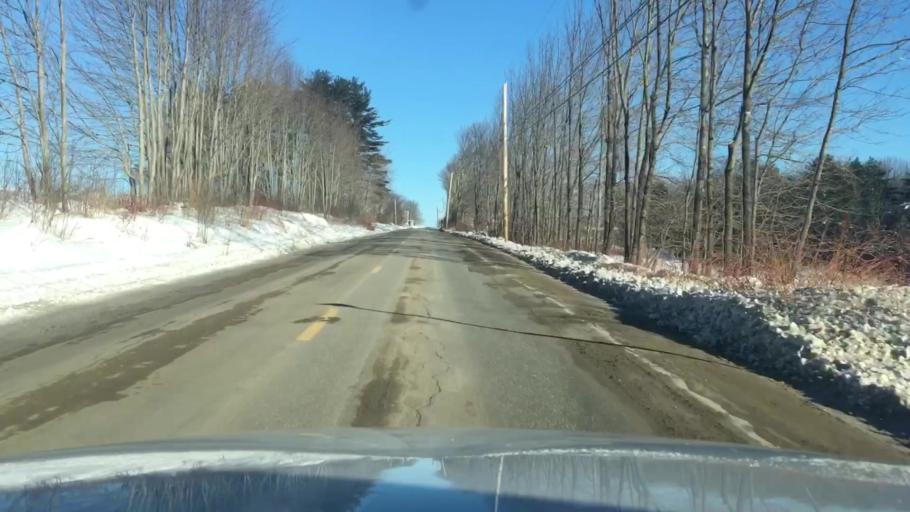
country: US
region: Maine
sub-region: Kennebec County
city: Mount Vernon
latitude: 44.4785
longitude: -69.9725
